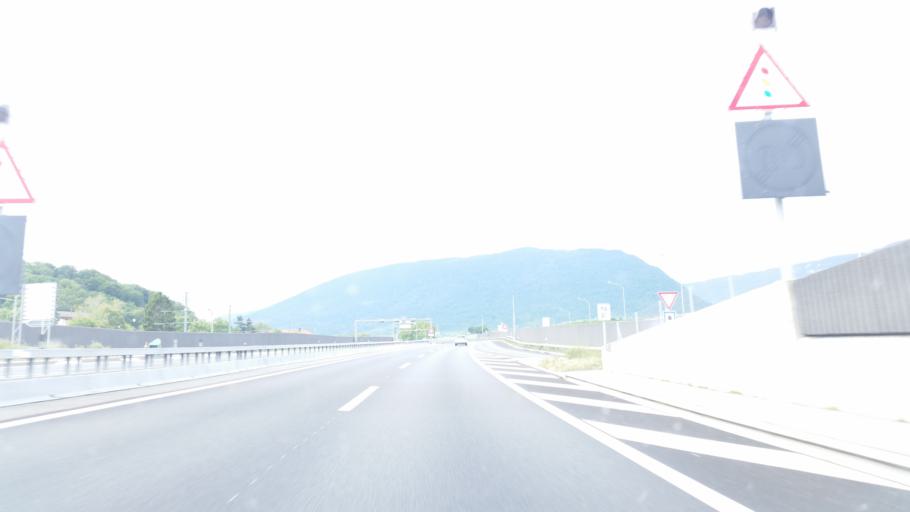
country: CH
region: Neuchatel
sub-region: Boudry District
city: Cortaillod
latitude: 46.9551
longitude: 6.8538
